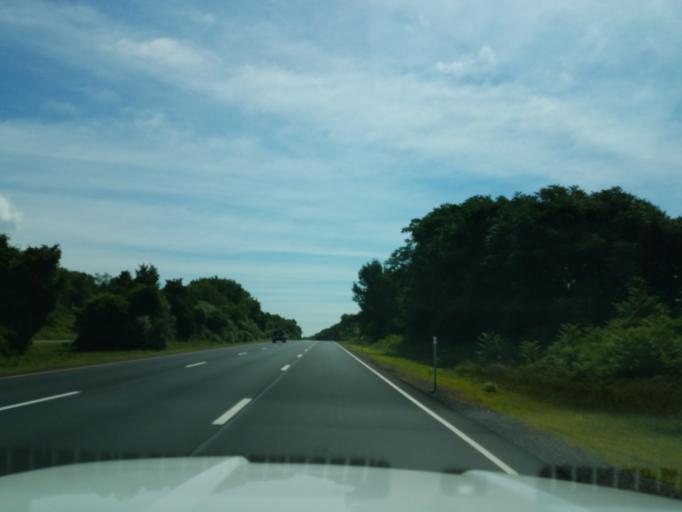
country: US
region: Connecticut
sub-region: New London County
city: Old Mystic
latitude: 41.3730
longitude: -71.9423
